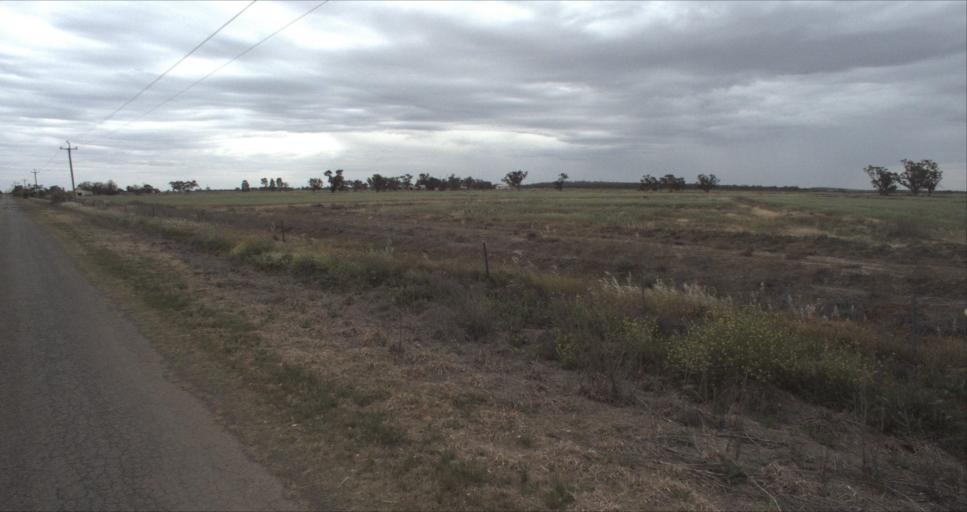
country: AU
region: New South Wales
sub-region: Leeton
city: Leeton
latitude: -34.4093
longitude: 146.3406
